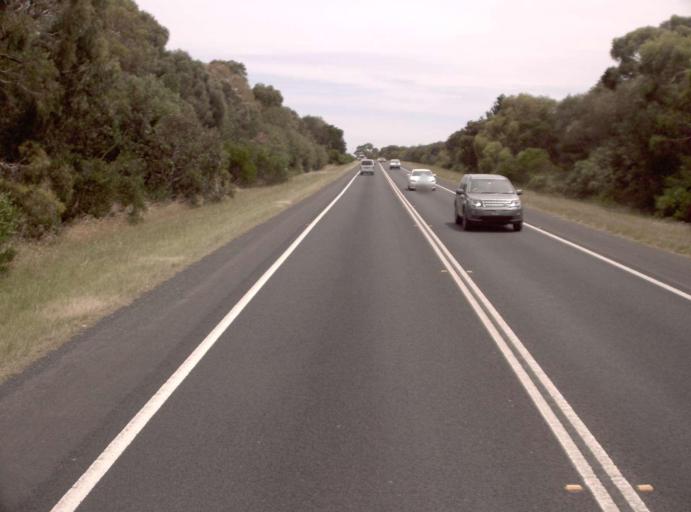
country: AU
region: Victoria
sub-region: Mornington Peninsula
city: Rosebud
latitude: -38.3740
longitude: 144.8967
